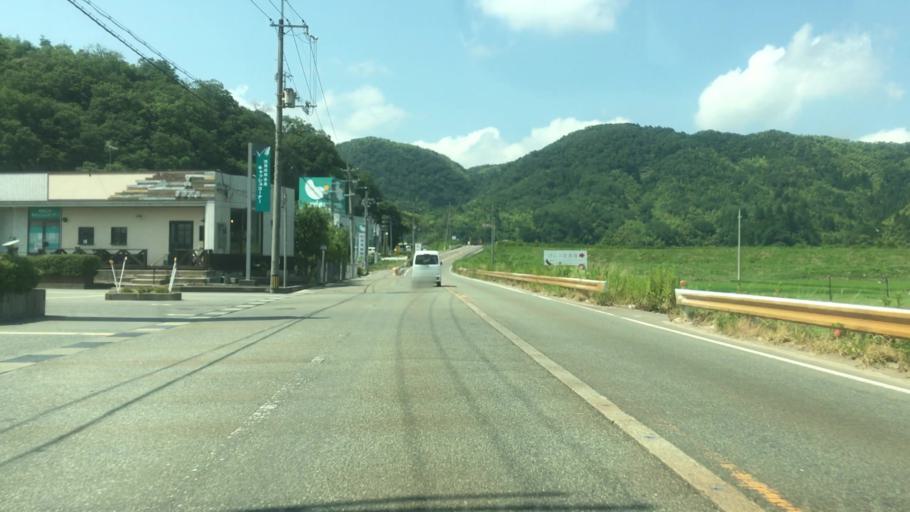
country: JP
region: Hyogo
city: Toyooka
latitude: 35.5608
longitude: 134.7960
